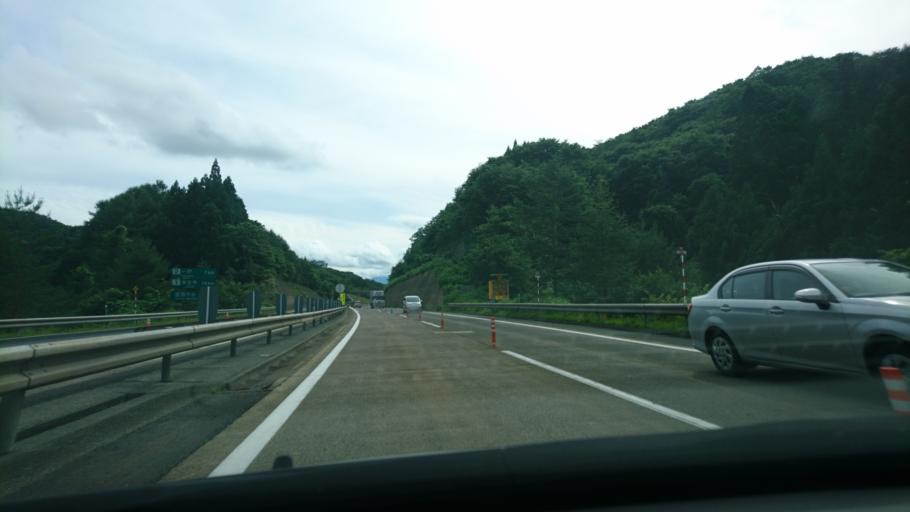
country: JP
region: Iwate
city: Ichinohe
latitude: 40.2283
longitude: 141.3706
